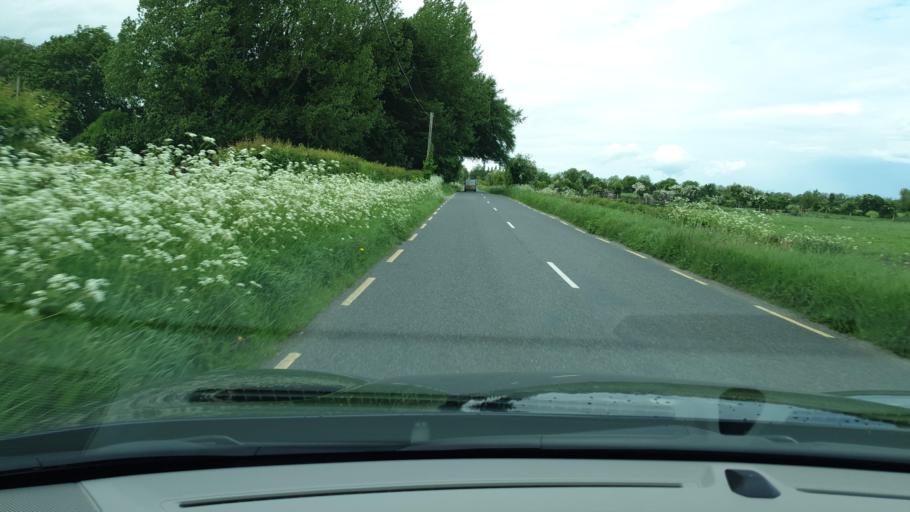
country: IE
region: Leinster
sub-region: An Mhi
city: Ratoath
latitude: 53.4841
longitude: -6.4322
